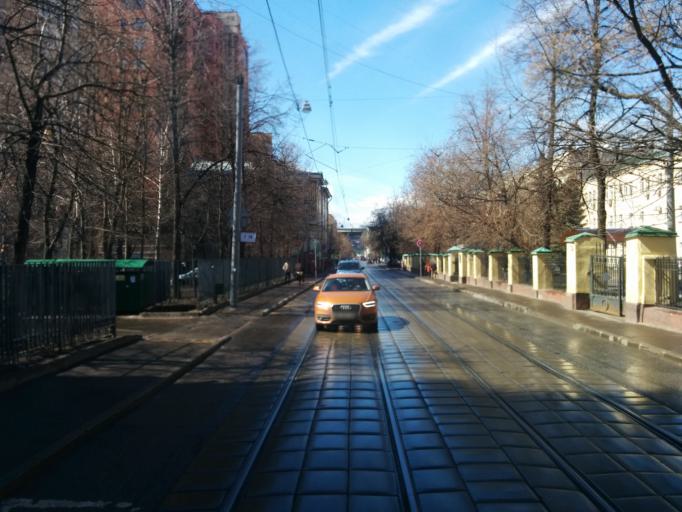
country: RU
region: Moscow
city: Mar'ina Roshcha
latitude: 55.7798
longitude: 37.6403
